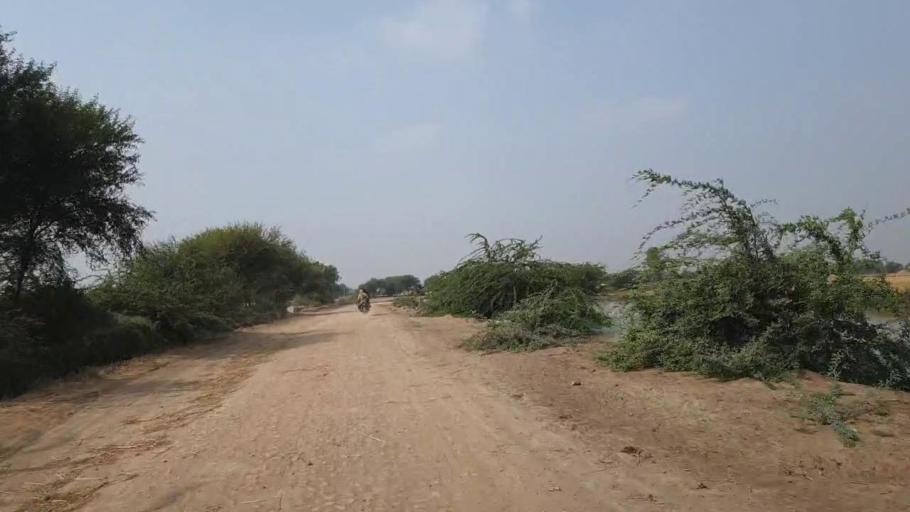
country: PK
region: Sindh
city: Kario
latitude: 24.7574
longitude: 68.5547
